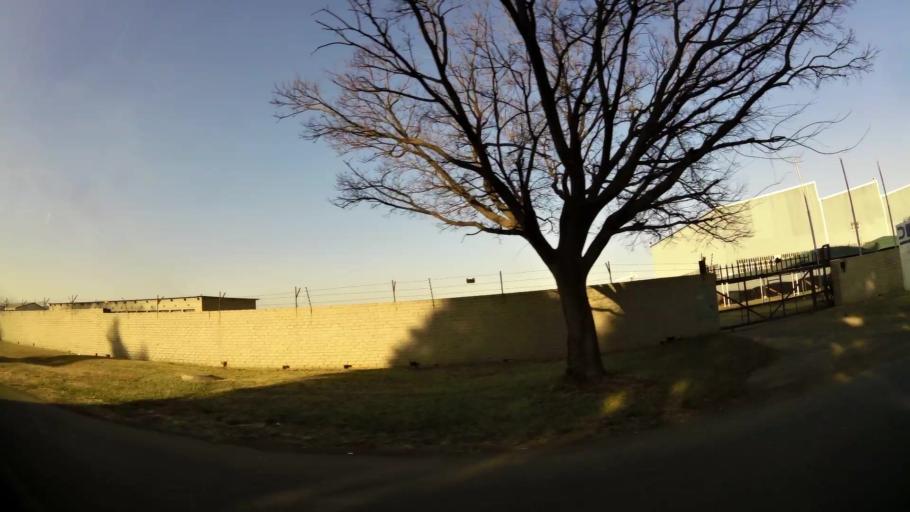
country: ZA
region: Gauteng
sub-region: West Rand District Municipality
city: Randfontein
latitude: -26.2000
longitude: 27.6835
